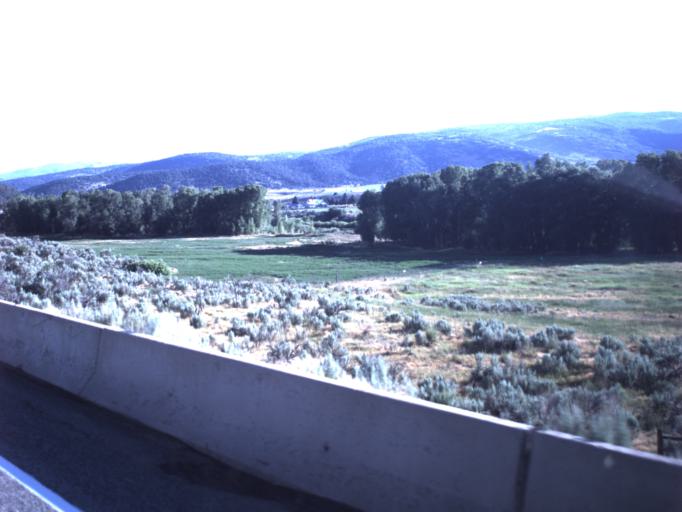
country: US
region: Utah
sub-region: Utah County
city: Woodland Hills
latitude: 39.9296
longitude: -111.5434
